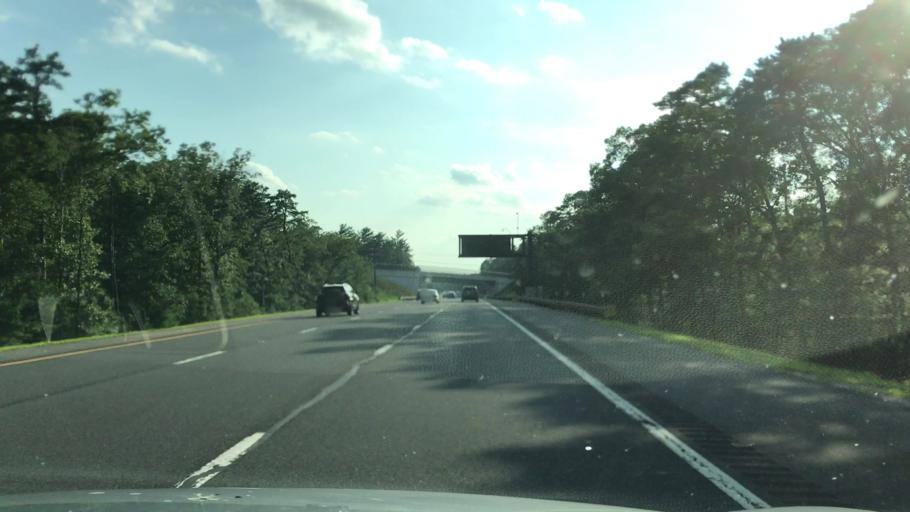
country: US
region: New Jersey
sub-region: Ocean County
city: Tuckerton
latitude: 39.6191
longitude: -74.4108
